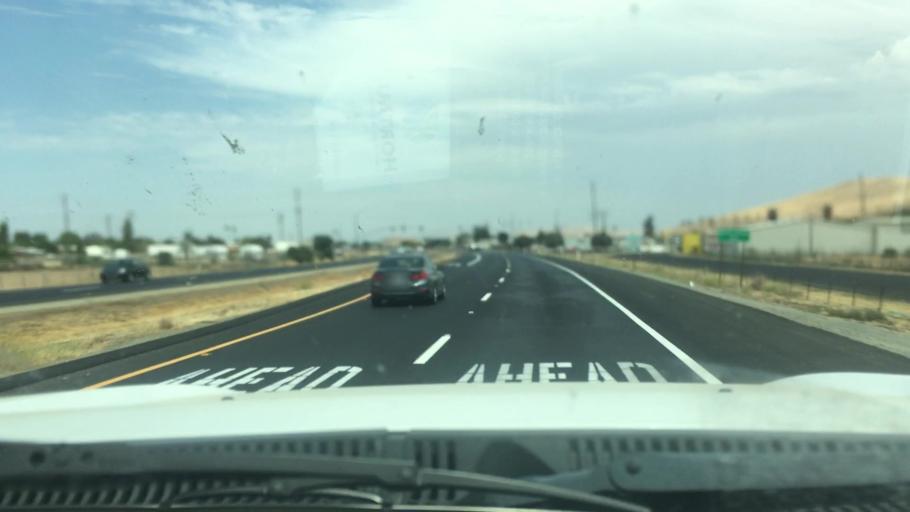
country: US
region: California
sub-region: Tulare County
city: Porterville
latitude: 36.0961
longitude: -119.0396
